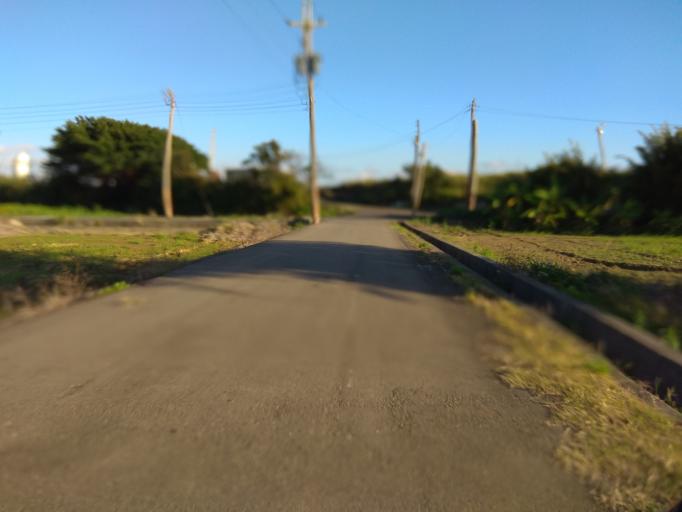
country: TW
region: Taiwan
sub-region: Hsinchu
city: Zhubei
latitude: 24.9892
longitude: 121.0429
